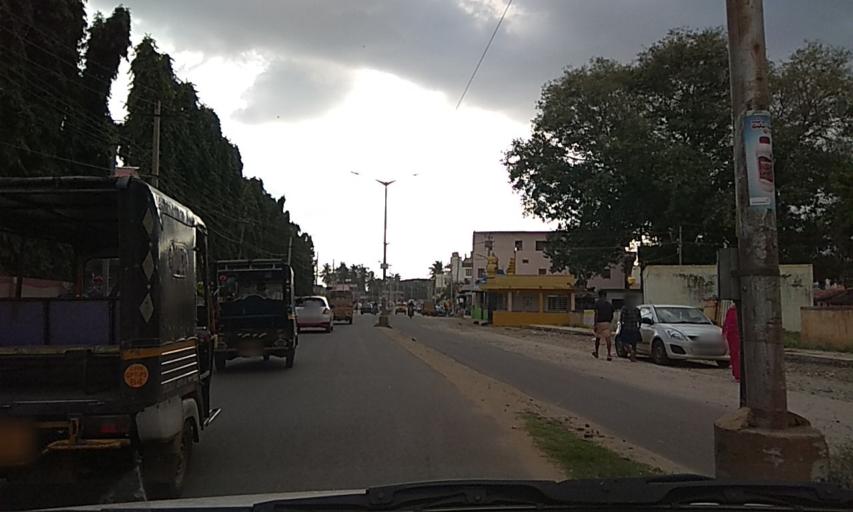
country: IN
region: Karnataka
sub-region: Chamrajnagar
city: Gundlupet
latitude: 11.8067
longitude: 76.6912
